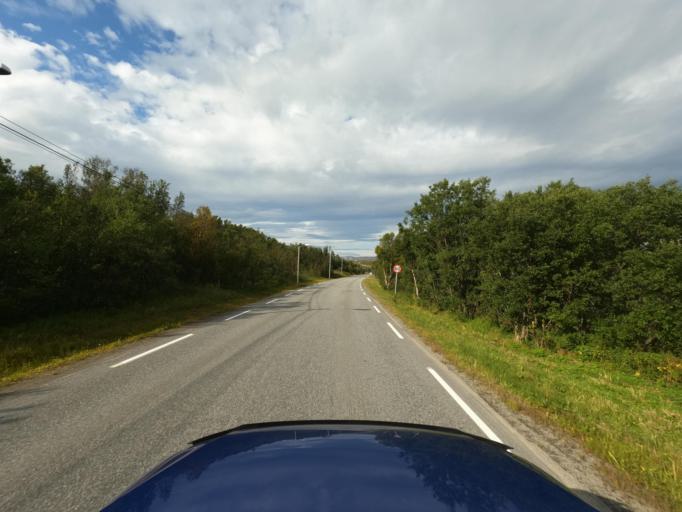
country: NO
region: Finnmark Fylke
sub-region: Kvalsund
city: Kvalsund
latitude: 70.5006
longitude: 24.0676
